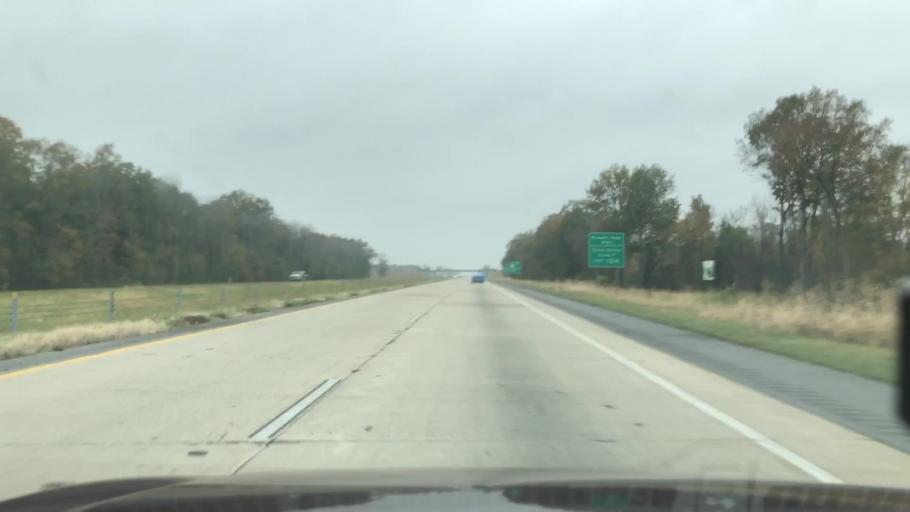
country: US
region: Louisiana
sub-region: Ouachita Parish
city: Lakeshore
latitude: 32.4884
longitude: -91.9822
